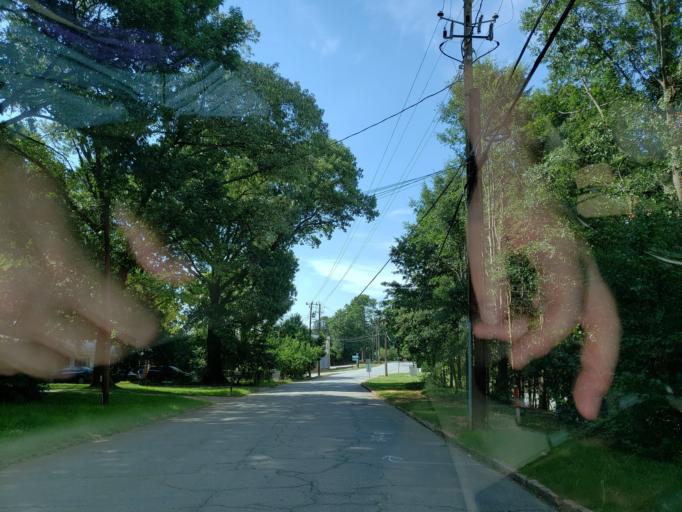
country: US
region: Georgia
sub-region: DeKalb County
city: Doraville
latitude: 33.8985
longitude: -84.2724
